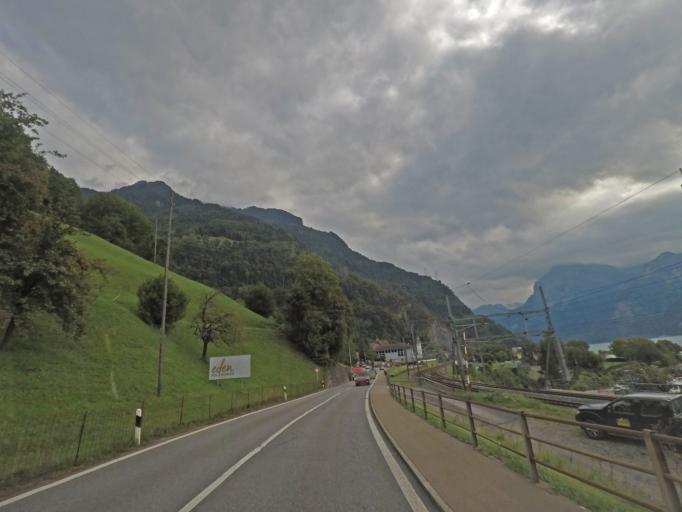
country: CH
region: Uri
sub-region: Uri
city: Bauen
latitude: 46.9530
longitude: 8.6212
